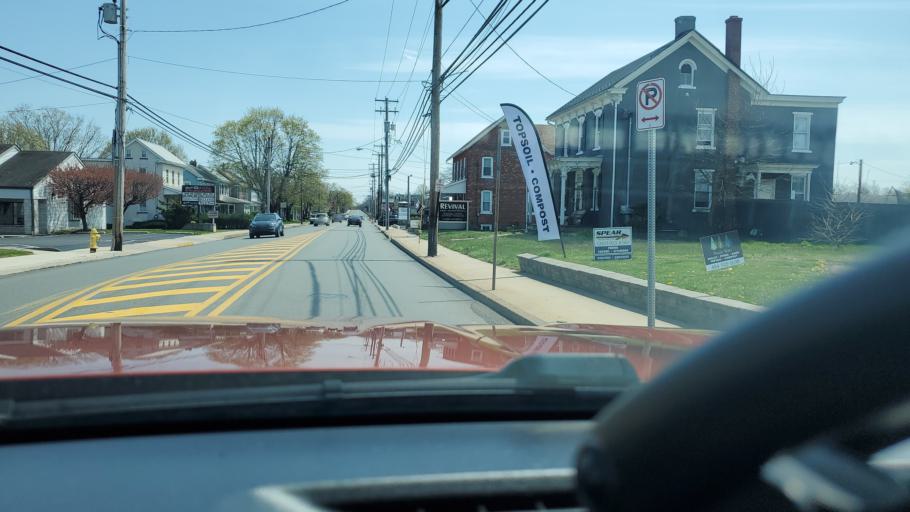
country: US
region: Pennsylvania
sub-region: Montgomery County
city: Pennsburg
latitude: 40.3904
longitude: -75.4917
